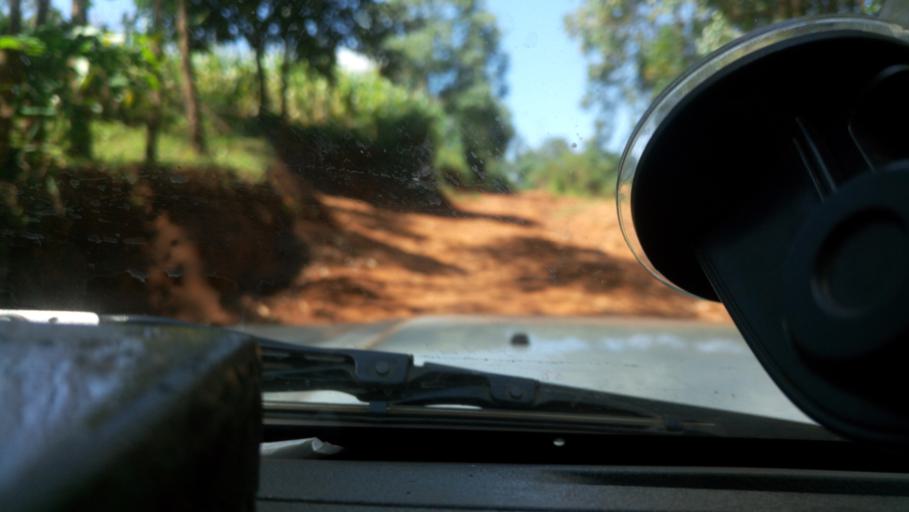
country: KE
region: Kisii
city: Ogembo
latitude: -0.8644
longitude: 34.7055
